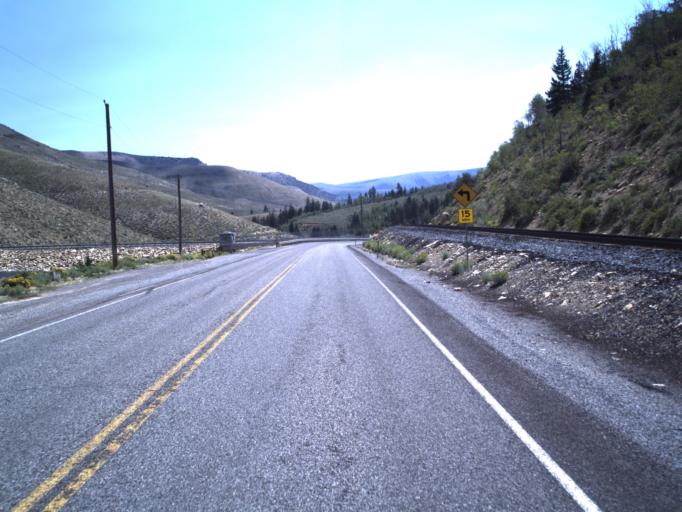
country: US
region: Utah
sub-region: Carbon County
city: Helper
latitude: 39.7866
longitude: -111.1232
